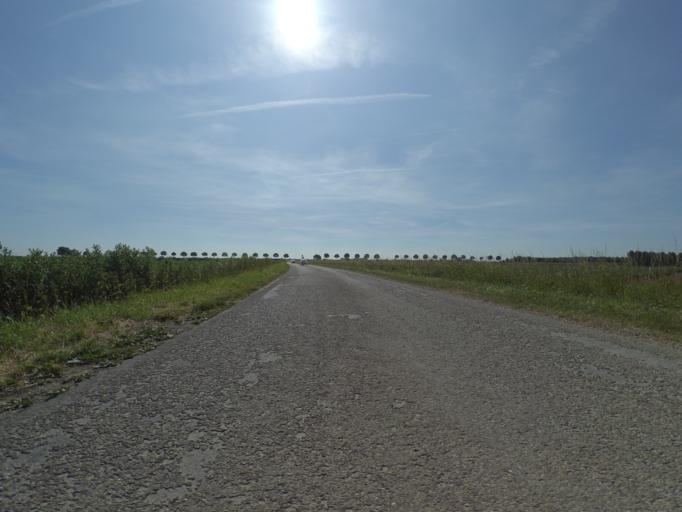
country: NL
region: Zeeland
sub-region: Gemeente Tholen
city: Tholen
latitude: 51.5577
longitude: 4.2377
